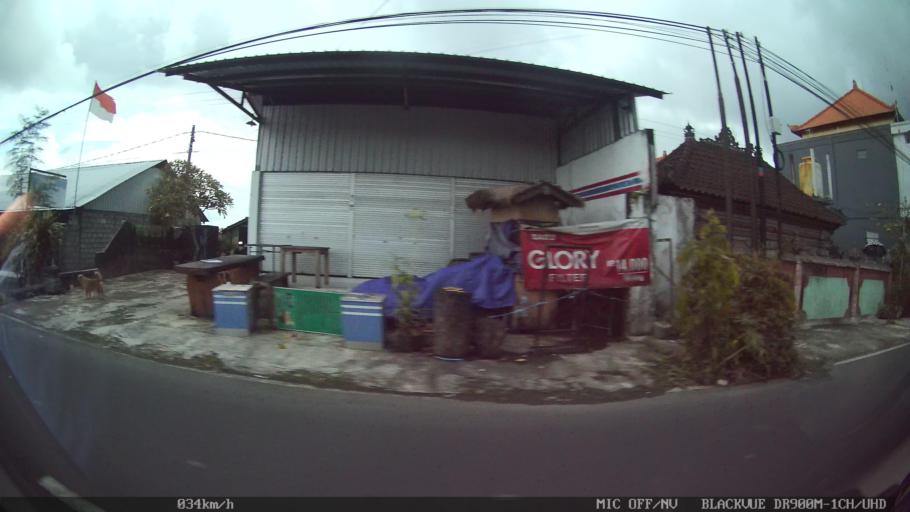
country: ID
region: Bali
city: Banjar Mambalkajanan
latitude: -8.5456
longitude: 115.2224
